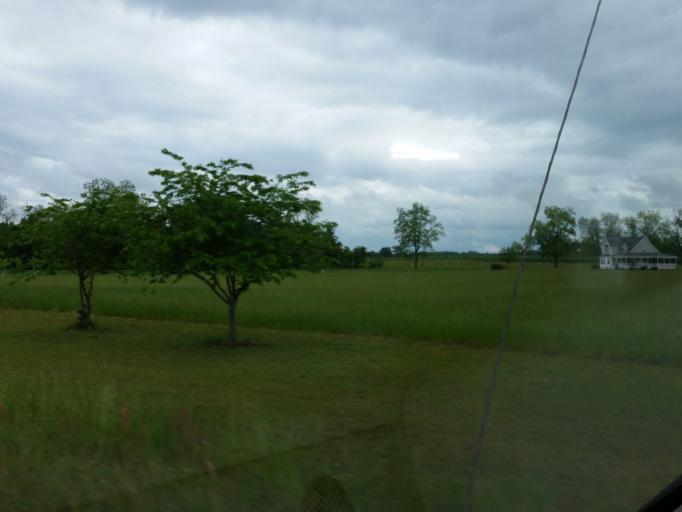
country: US
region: Georgia
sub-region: Peach County
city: Byron
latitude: 32.6751
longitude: -83.8376
